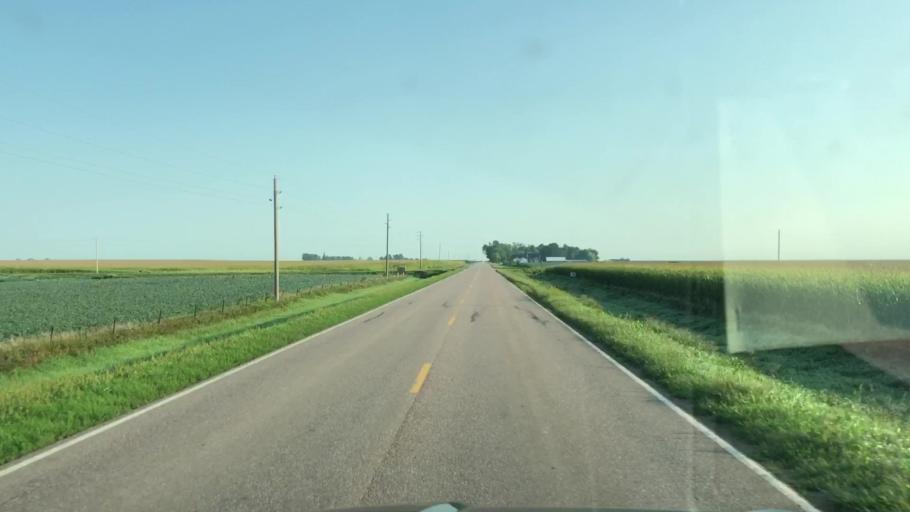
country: US
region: Iowa
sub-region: Sioux County
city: Hull
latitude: 43.1990
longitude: -96.0004
